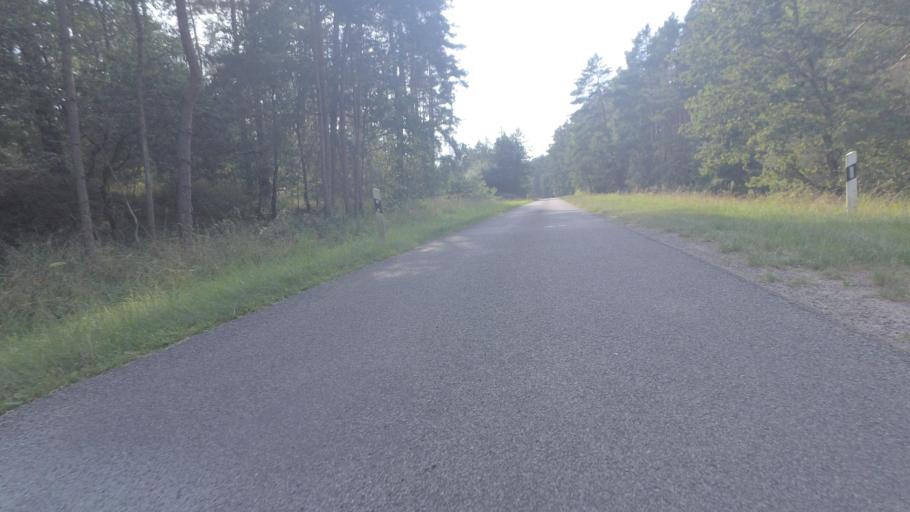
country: DE
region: Brandenburg
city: Wittstock
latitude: 53.2800
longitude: 12.4937
